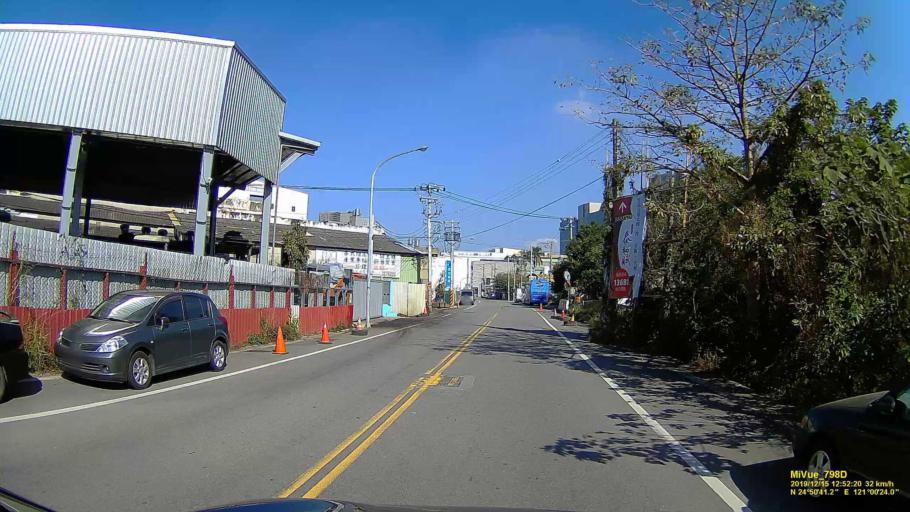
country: TW
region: Taiwan
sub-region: Hsinchu
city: Zhubei
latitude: 24.8446
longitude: 121.0067
